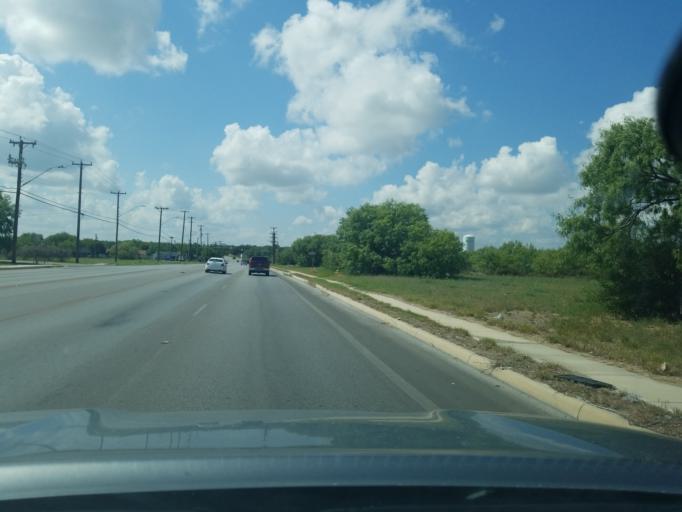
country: US
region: Texas
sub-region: Bexar County
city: San Antonio
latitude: 29.3377
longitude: -98.5342
